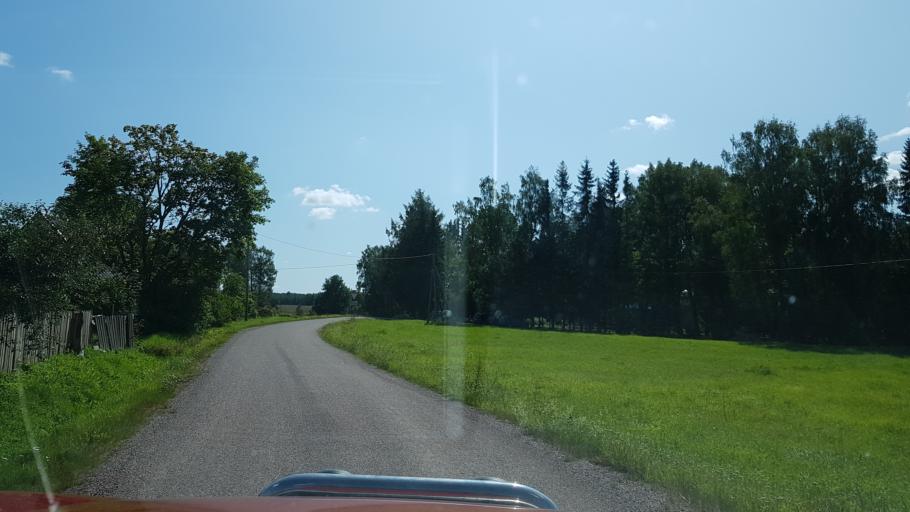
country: RU
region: Pskov
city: Pechory
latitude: 57.7108
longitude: 27.3947
